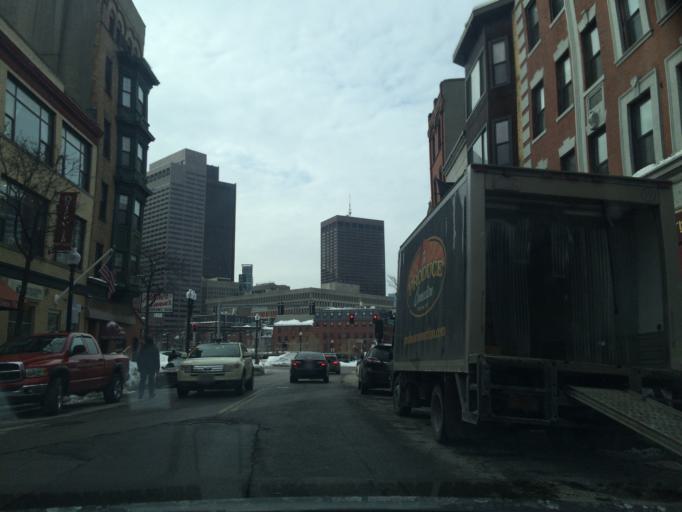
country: US
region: Massachusetts
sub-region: Suffolk County
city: Boston
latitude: 42.3631
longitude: -71.0551
